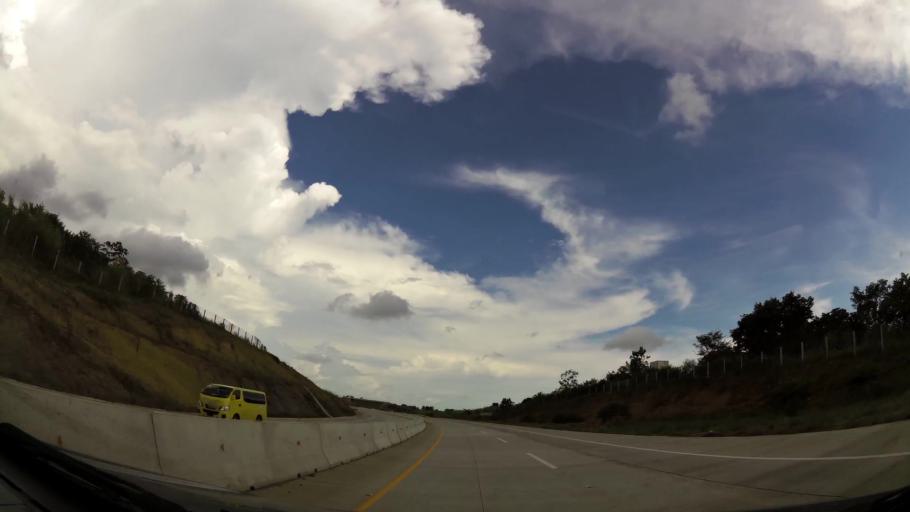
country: PA
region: Panama
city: Tocumen
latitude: 9.1054
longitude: -79.3989
